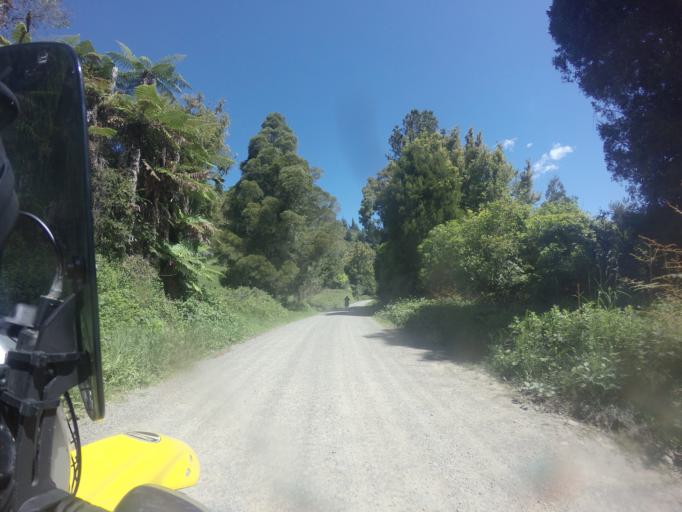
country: NZ
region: Bay of Plenty
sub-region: Opotiki District
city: Opotiki
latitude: -38.2876
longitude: 177.3443
